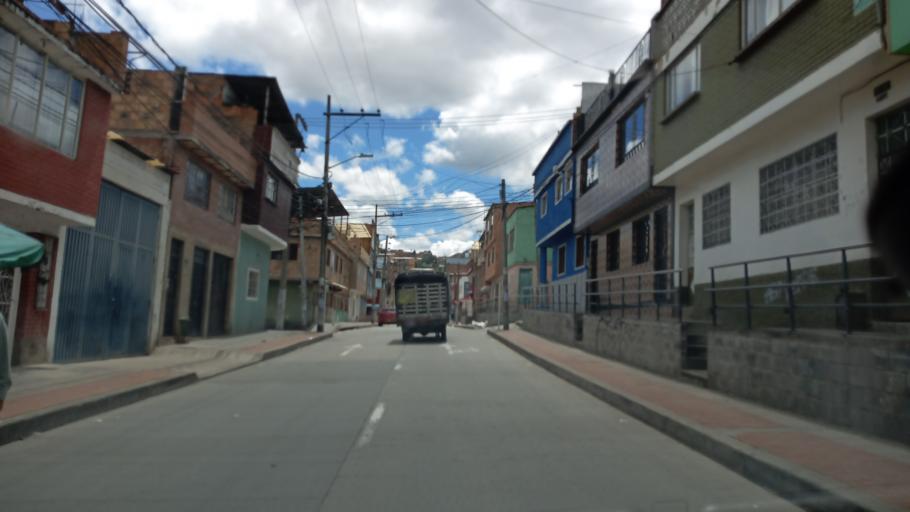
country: CO
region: Bogota D.C.
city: Bogota
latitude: 4.5675
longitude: -74.1168
